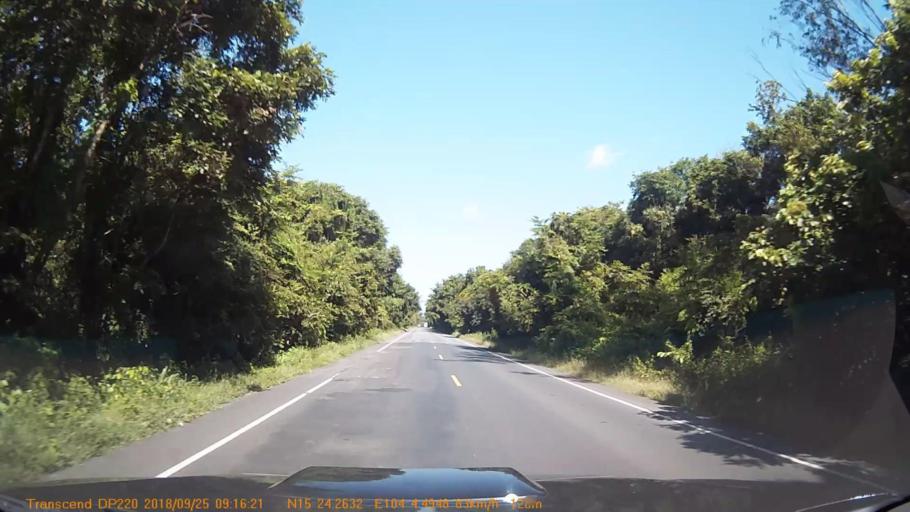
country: TH
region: Sisaket
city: Sila Lat
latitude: 15.4043
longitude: 104.0750
